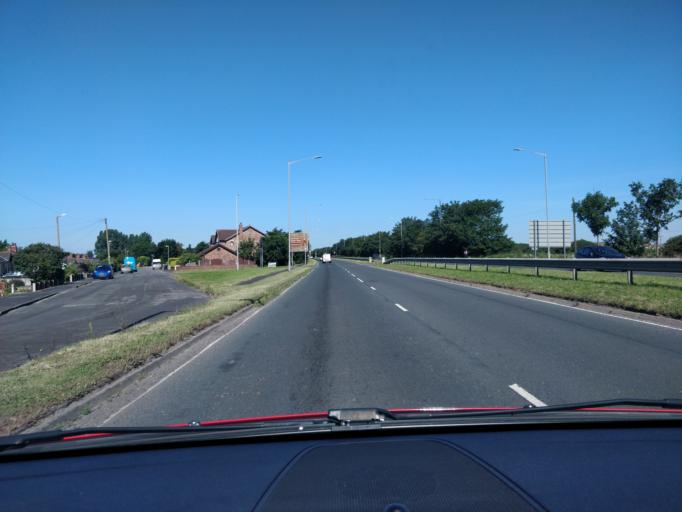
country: GB
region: England
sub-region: Lancashire
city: Banks
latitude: 53.6737
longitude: -2.9253
